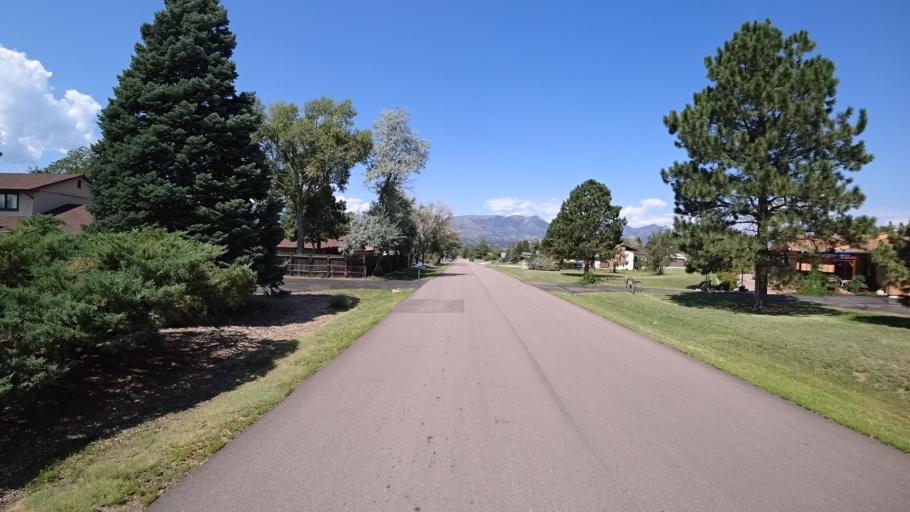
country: US
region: Colorado
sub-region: El Paso County
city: Air Force Academy
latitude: 38.9396
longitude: -104.7879
